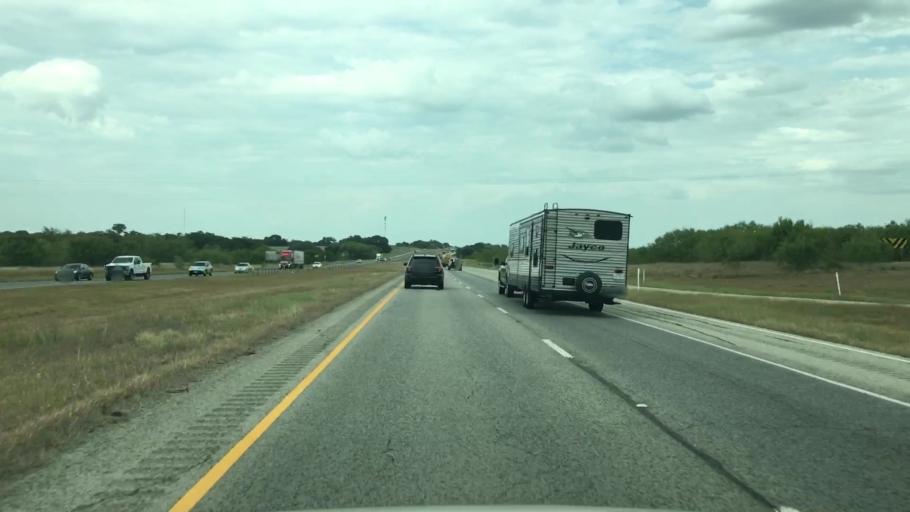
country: US
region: Texas
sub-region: Atascosa County
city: Pleasanton
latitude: 29.1094
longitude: -98.4321
